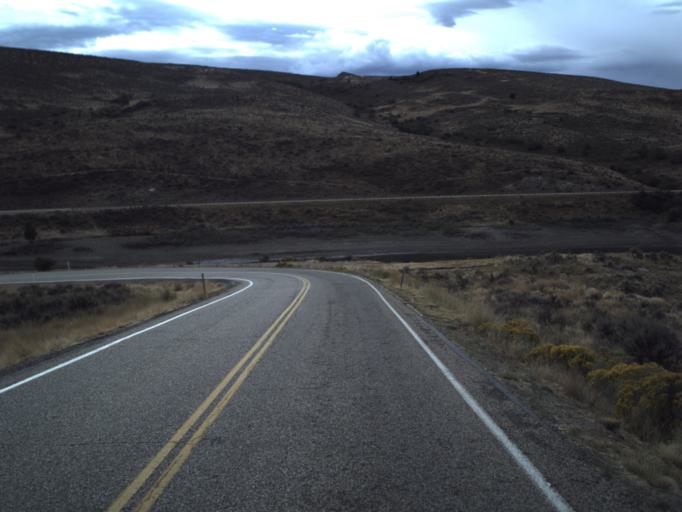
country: US
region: Utah
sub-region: Morgan County
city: Morgan
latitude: 40.9216
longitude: -111.5809
